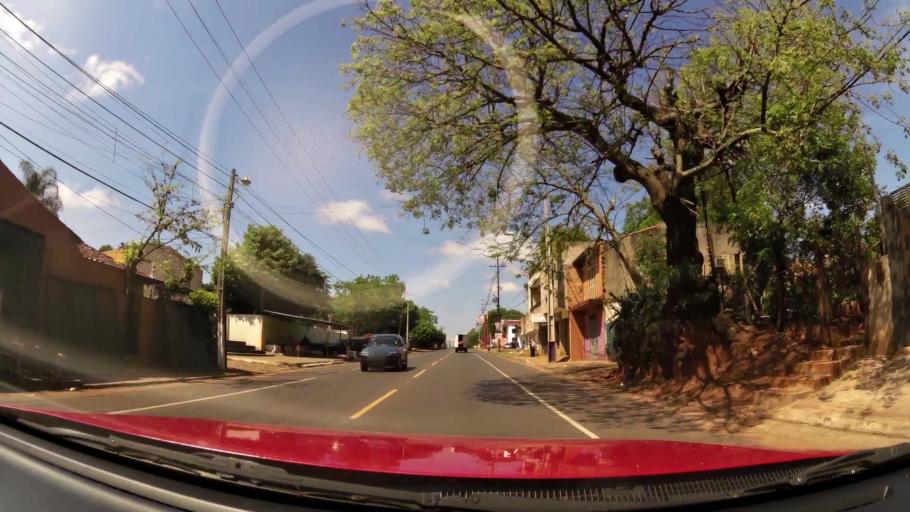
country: PY
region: Central
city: San Lorenzo
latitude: -25.3119
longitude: -57.5064
